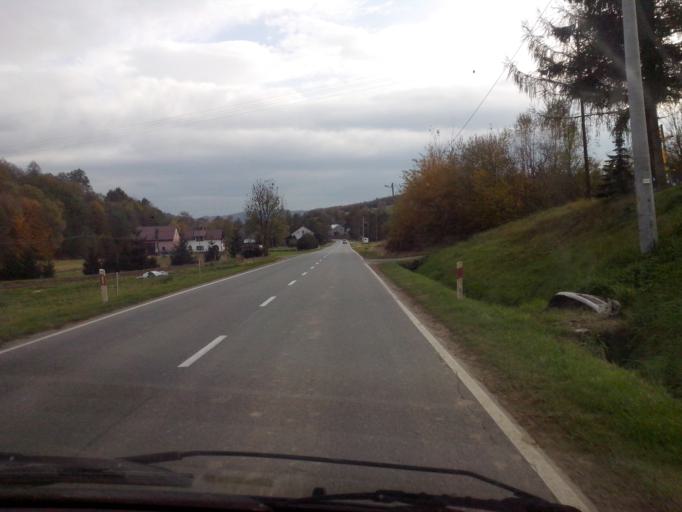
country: PL
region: Subcarpathian Voivodeship
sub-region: Powiat strzyzowski
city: Wisniowa
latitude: 49.8927
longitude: 21.6434
